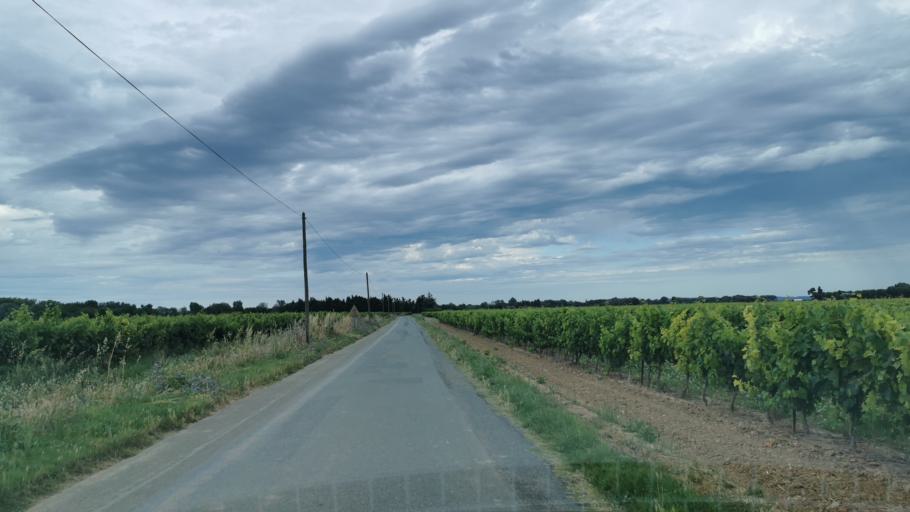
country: FR
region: Languedoc-Roussillon
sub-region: Departement de l'Aude
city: Moussan
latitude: 43.2448
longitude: 2.9705
